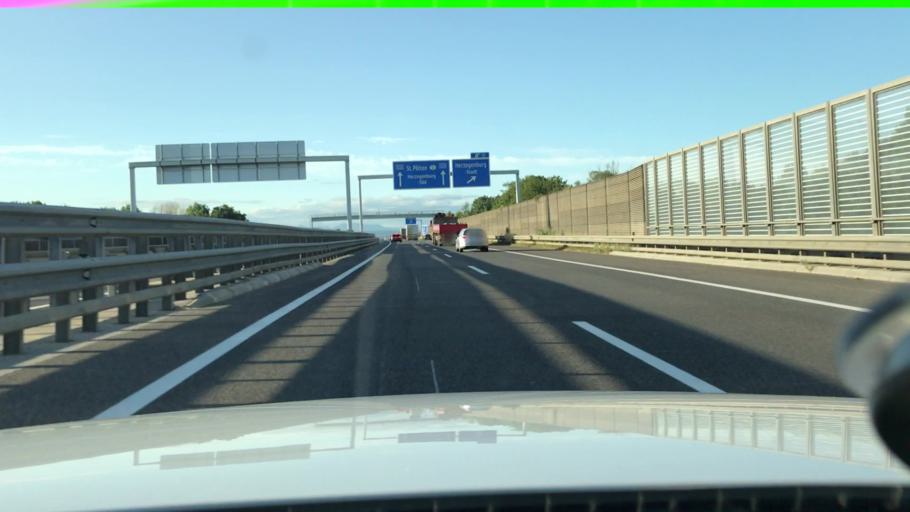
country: AT
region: Lower Austria
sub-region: Politischer Bezirk Sankt Polten
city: Herzogenburg
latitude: 48.2888
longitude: 15.7023
